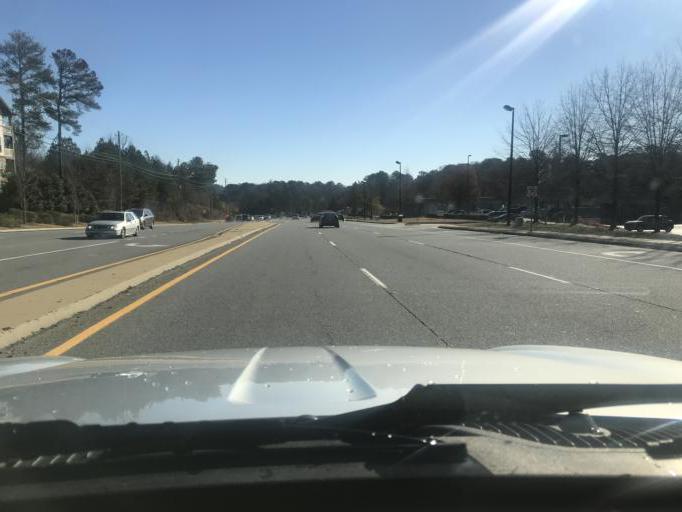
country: US
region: Georgia
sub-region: Gwinnett County
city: Duluth
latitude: 33.9768
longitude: -84.0784
